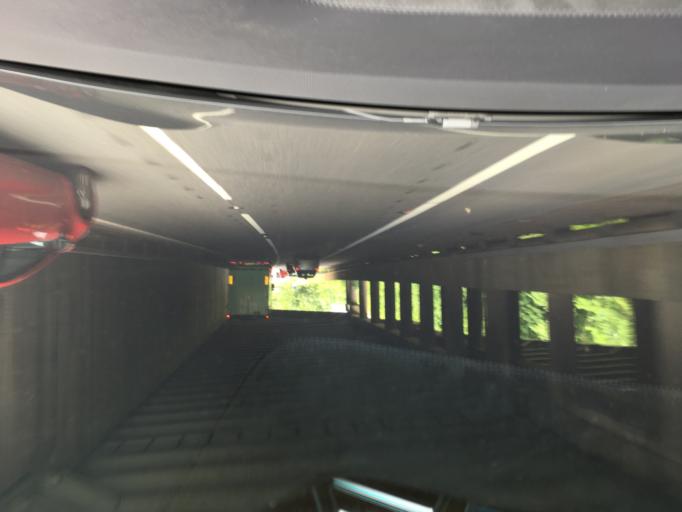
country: GB
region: England
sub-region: Manchester
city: Didsbury
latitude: 53.3990
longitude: -2.2380
